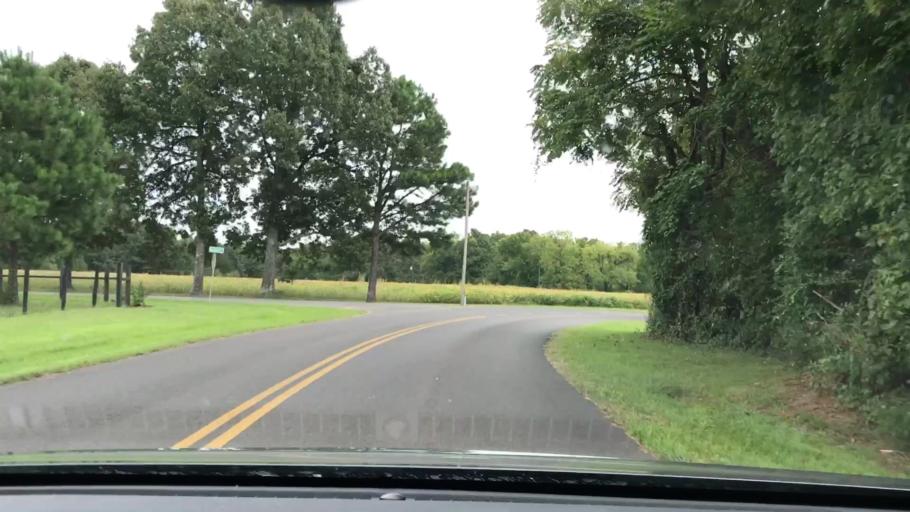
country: US
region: Kentucky
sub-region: Marshall County
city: Benton
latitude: 36.8323
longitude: -88.3694
